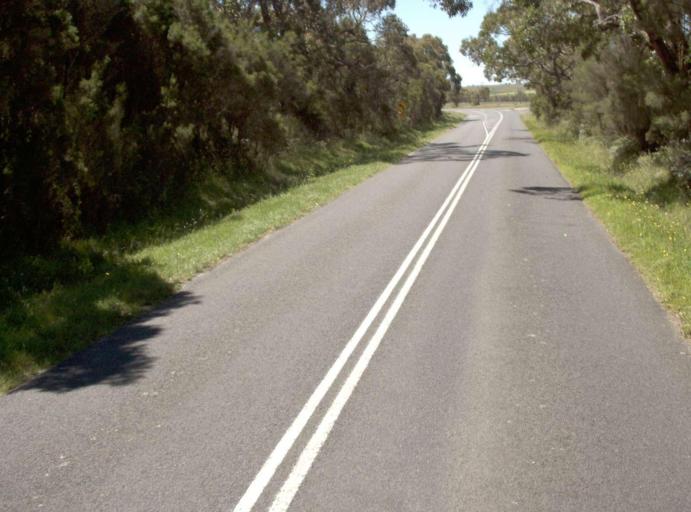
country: AU
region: Victoria
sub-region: Bass Coast
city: North Wonthaggi
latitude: -38.7927
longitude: 146.0869
